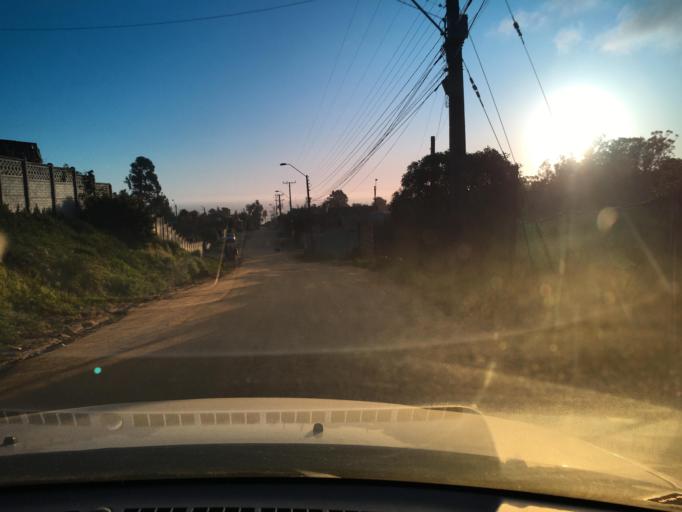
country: CL
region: Valparaiso
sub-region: San Antonio Province
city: El Tabo
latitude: -33.4537
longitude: -71.6552
